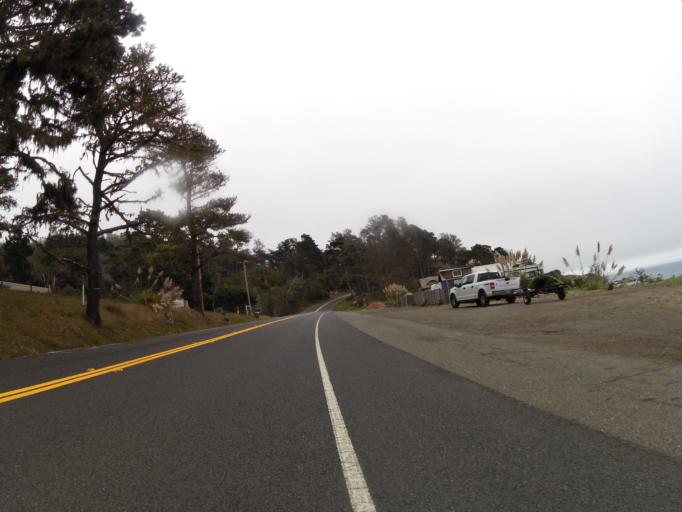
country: US
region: California
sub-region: Sonoma County
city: Sea Ranch
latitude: 38.5329
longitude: -123.2721
